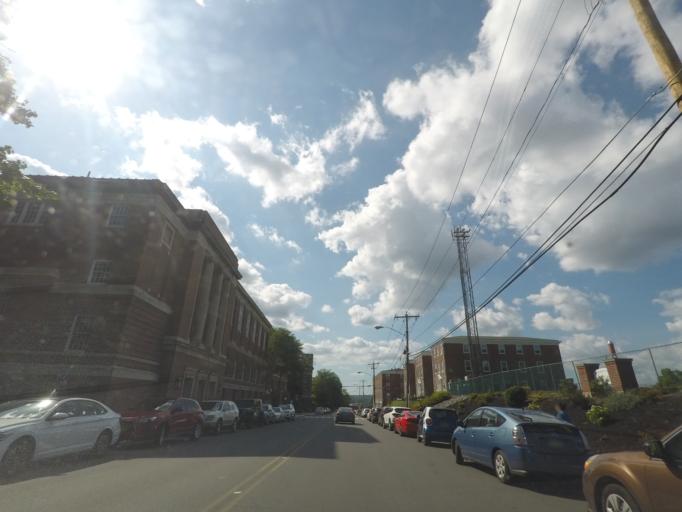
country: US
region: New York
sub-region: Rensselaer County
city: Troy
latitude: 42.7310
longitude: -73.6784
